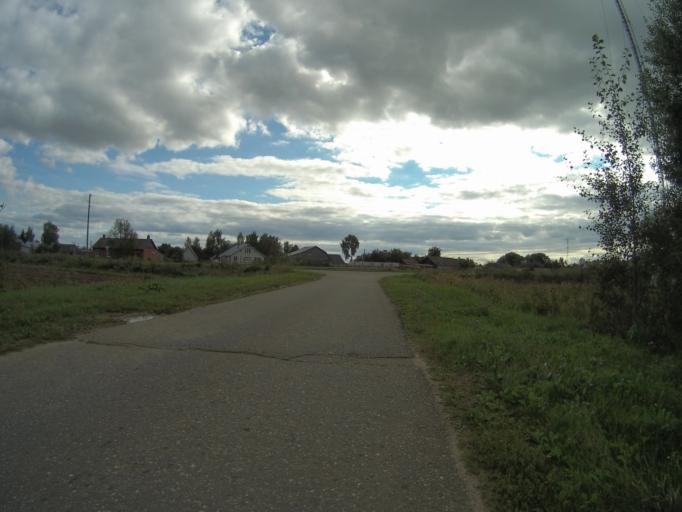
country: RU
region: Vladimir
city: Orgtrud
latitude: 56.3145
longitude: 40.6130
